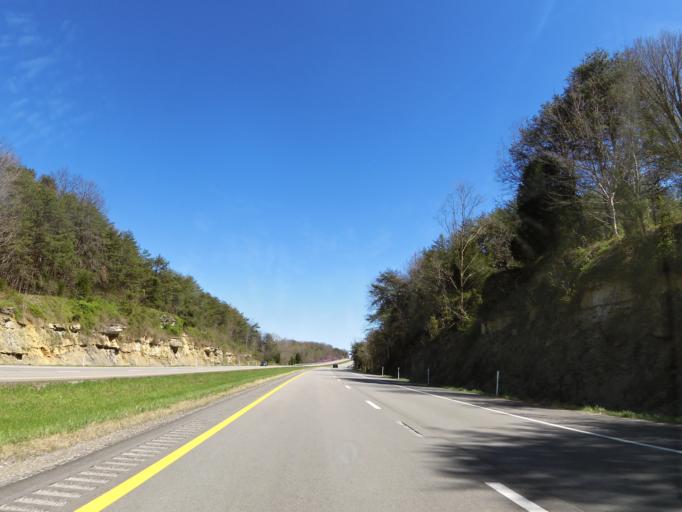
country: US
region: Kentucky
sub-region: Pulaski County
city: Somerset
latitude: 37.0972
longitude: -84.8311
